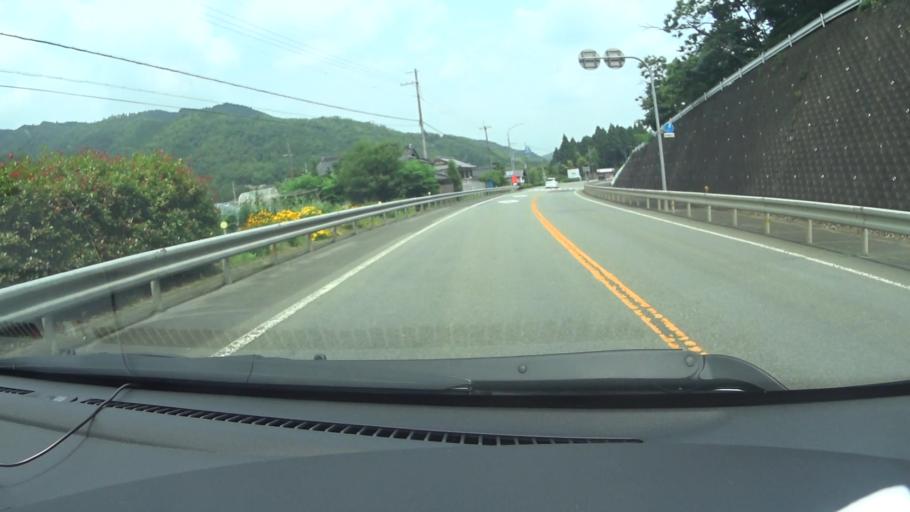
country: JP
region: Kyoto
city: Ayabe
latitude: 35.2780
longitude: 135.3355
